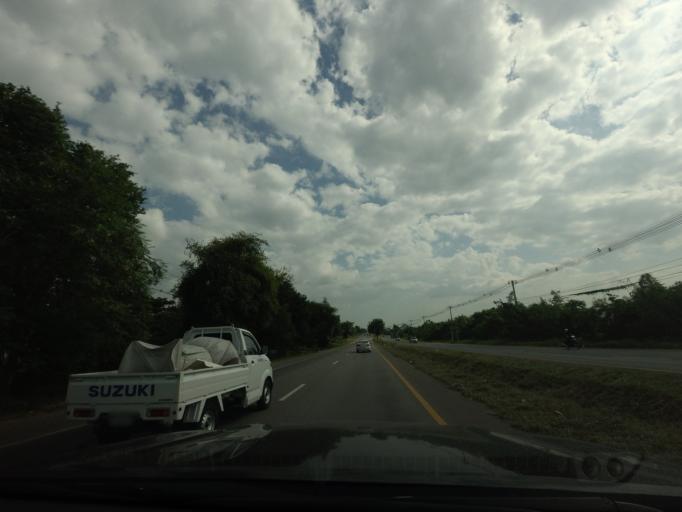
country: TH
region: Lop Buri
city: Chai Badan
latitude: 15.2576
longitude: 101.1252
